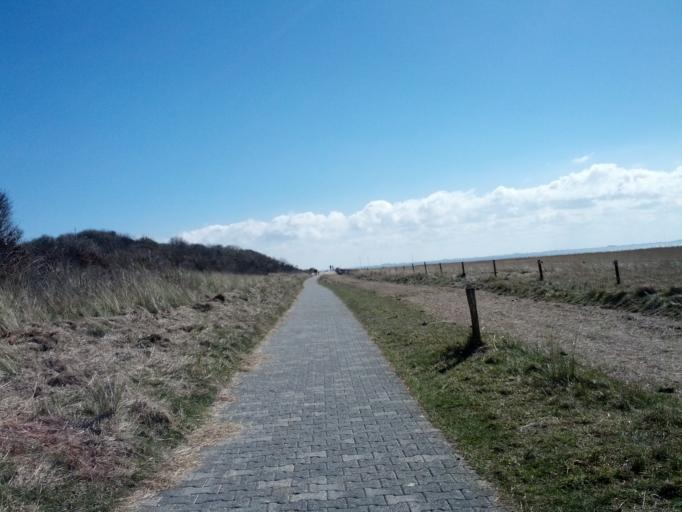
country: DE
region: Lower Saxony
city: Spiekeroog
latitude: 53.7482
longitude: 7.6175
